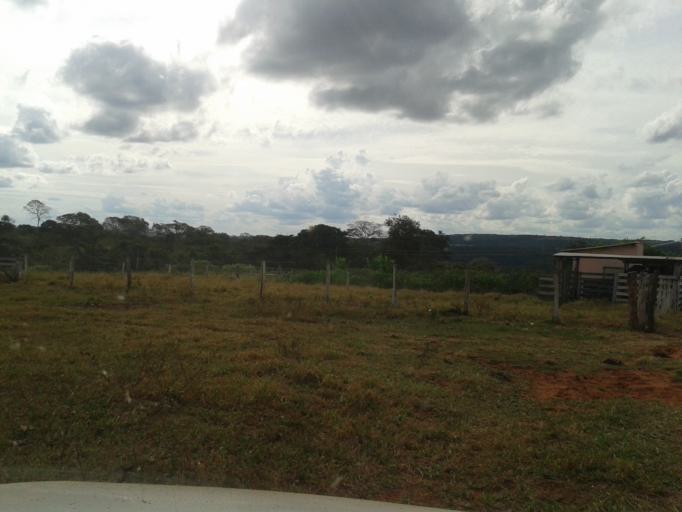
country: BR
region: Minas Gerais
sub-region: Campina Verde
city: Campina Verde
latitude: -19.4455
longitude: -49.6126
